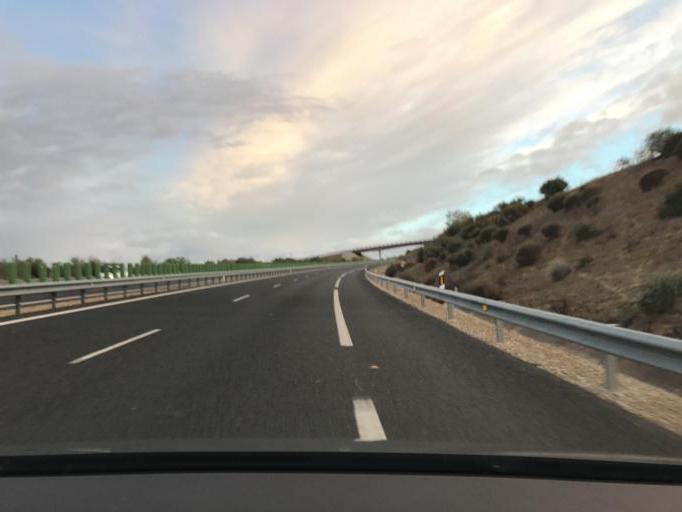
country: ES
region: Andalusia
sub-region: Provincia de Jaen
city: Jaen
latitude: 37.8162
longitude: -3.7368
